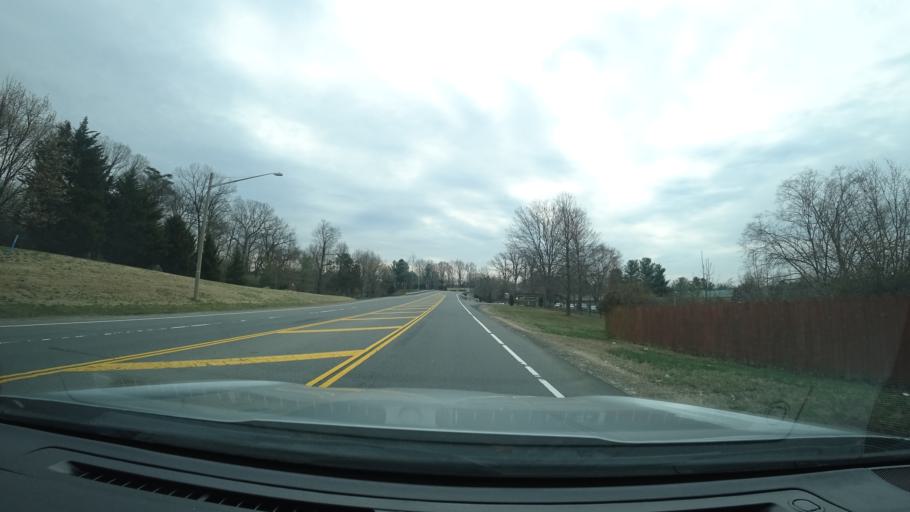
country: US
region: Virginia
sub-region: Fairfax County
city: Reston
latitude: 38.9733
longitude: -77.3138
